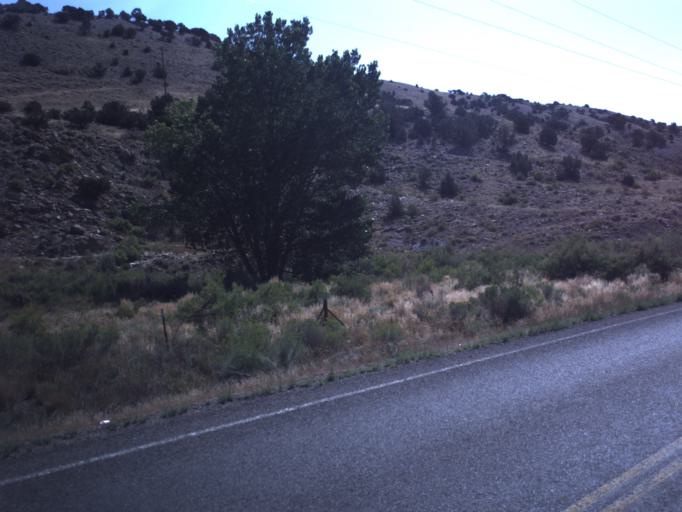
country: US
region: Utah
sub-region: Duchesne County
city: Duchesne
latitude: 40.2697
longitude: -110.4214
